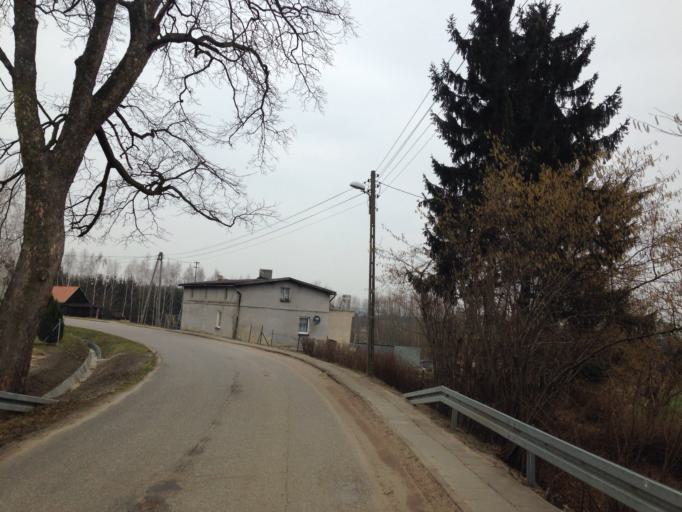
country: PL
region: Pomeranian Voivodeship
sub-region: Powiat kwidzynski
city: Sadlinki
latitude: 53.7377
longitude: 18.8264
